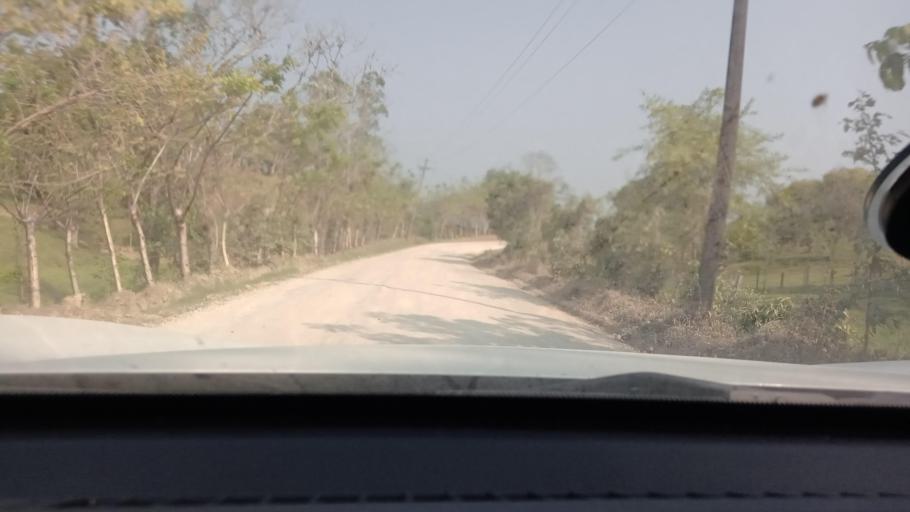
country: MX
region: Tabasco
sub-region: Huimanguillo
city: Francisco Rueda
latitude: 17.6194
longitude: -93.9413
